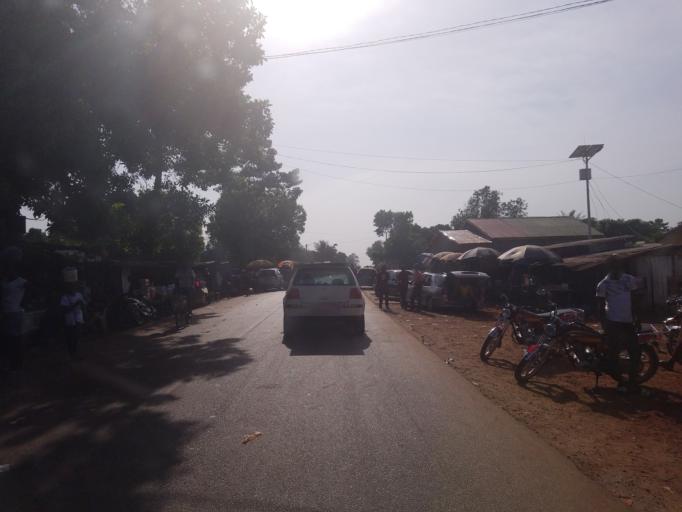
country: GN
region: Boke
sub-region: Boffa
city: Boffa
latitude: 10.1895
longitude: -14.0409
